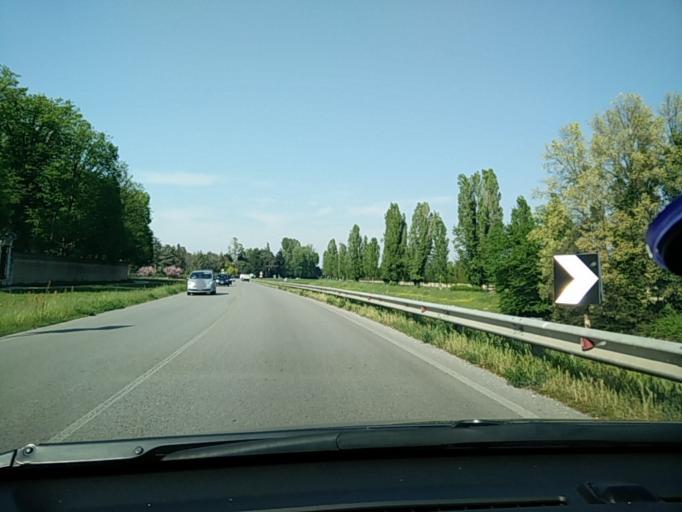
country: IT
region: Veneto
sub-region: Provincia di Venezia
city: Stra
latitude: 45.4085
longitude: 12.0137
